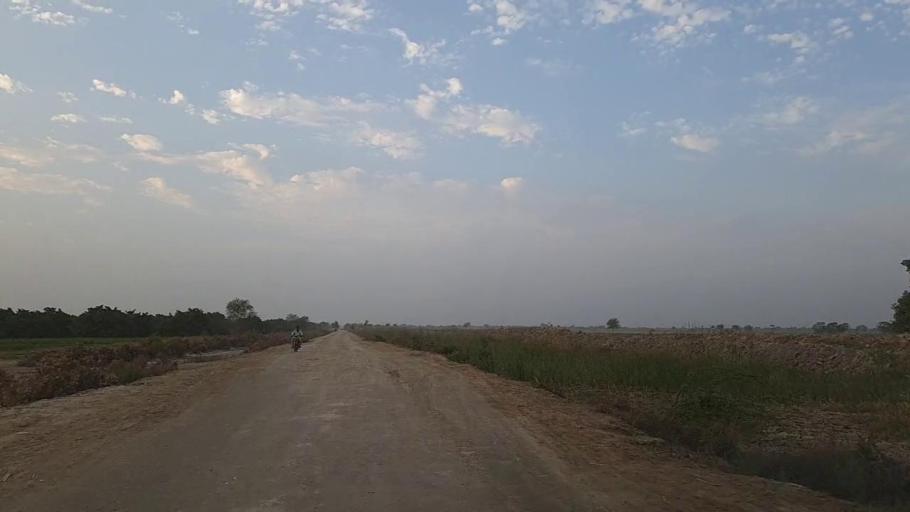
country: PK
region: Sindh
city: Mirwah Gorchani
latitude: 25.3273
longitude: 69.2155
